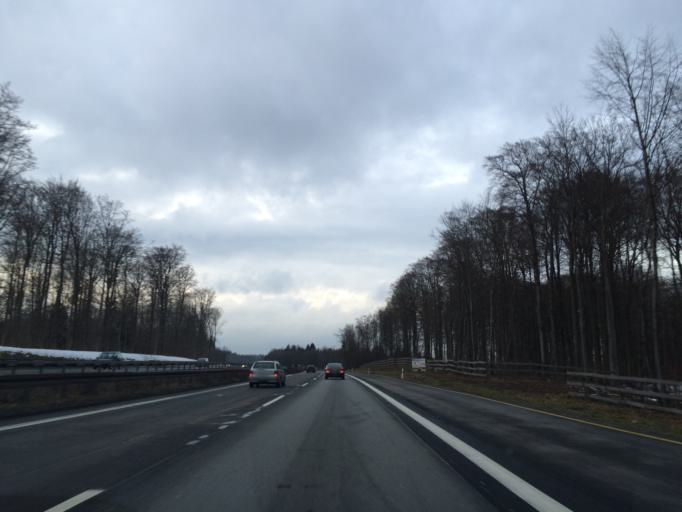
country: DE
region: Bavaria
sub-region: Regierungsbezirk Unterfranken
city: Weibersbrunn
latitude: 49.9104
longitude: 9.3691
